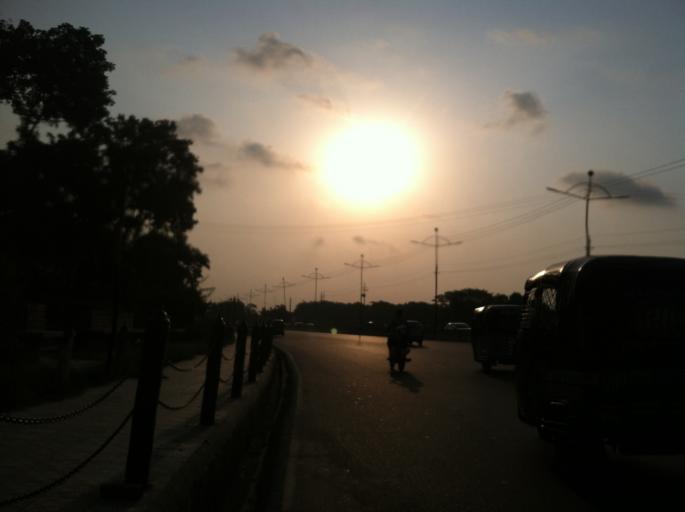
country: BD
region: Dhaka
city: Tungi
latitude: 23.8172
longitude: 90.4116
